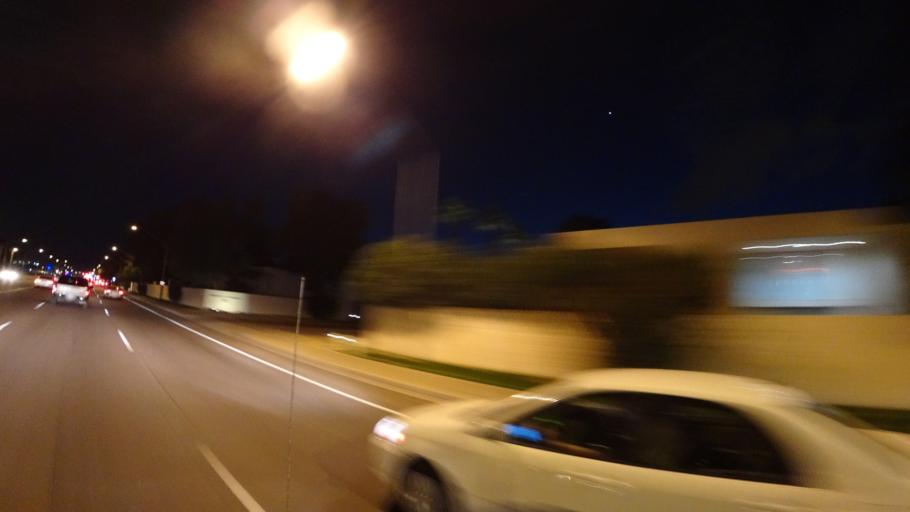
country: US
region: Arizona
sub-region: Maricopa County
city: Tempe
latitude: 33.3982
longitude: -111.8746
